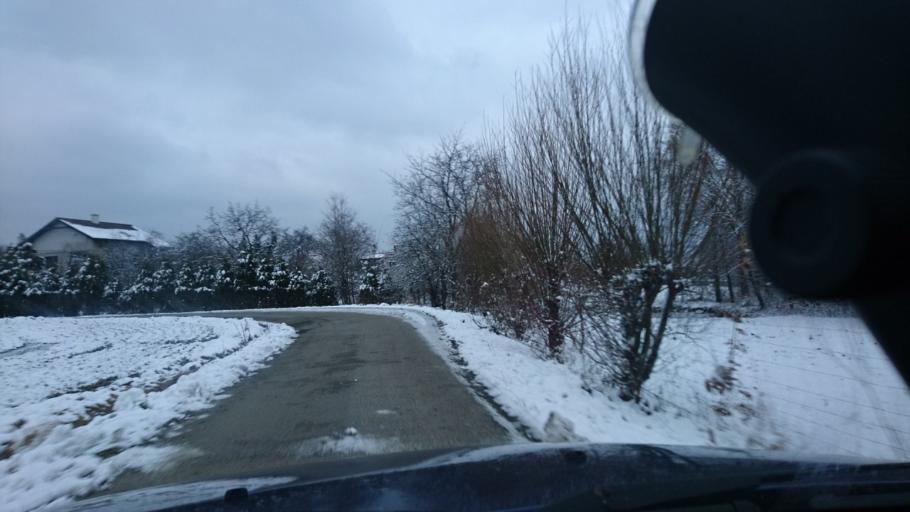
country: PL
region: Silesian Voivodeship
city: Janowice
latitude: 49.8642
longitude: 19.1102
